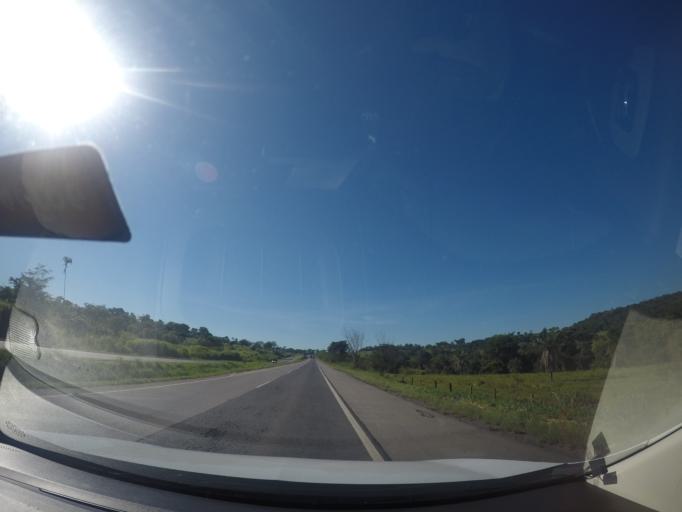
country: BR
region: Goias
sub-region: Pontalina
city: Pontalina
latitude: -17.4723
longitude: -49.2161
